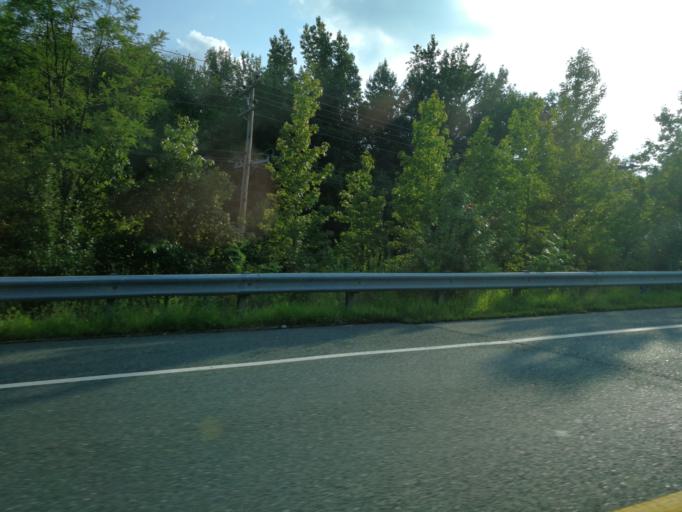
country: US
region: Maryland
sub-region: Harford County
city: Perryman
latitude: 39.4905
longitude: -76.2023
